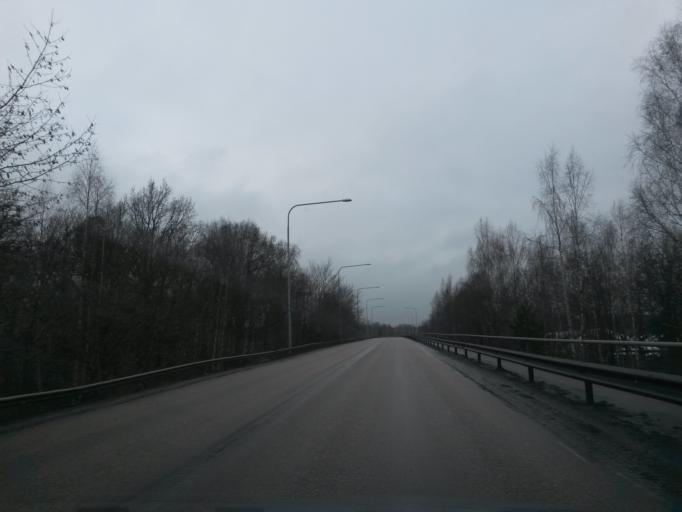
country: SE
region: Vaestra Goetaland
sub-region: Vanersborgs Kommun
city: Vargon
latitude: 58.3586
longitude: 12.3848
